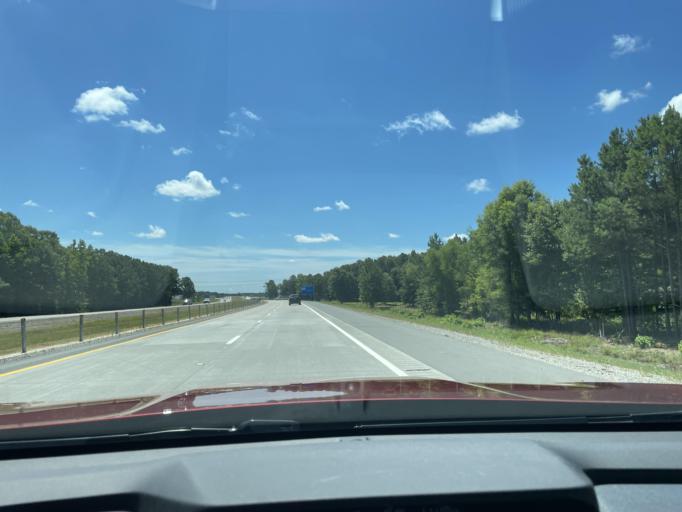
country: US
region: Arkansas
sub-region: Jefferson County
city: White Hall
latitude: 34.2357
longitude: -92.0854
